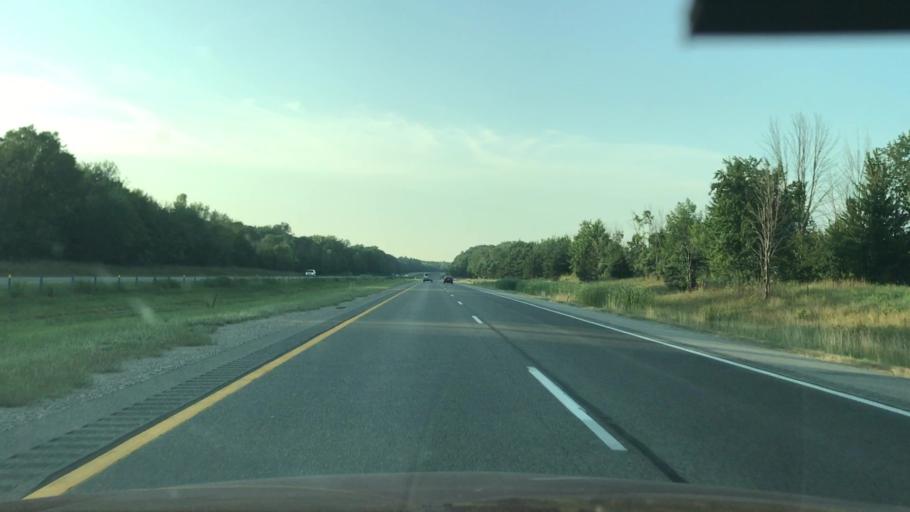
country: US
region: Michigan
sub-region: Allegan County
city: Douglas
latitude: 42.5575
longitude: -86.2195
